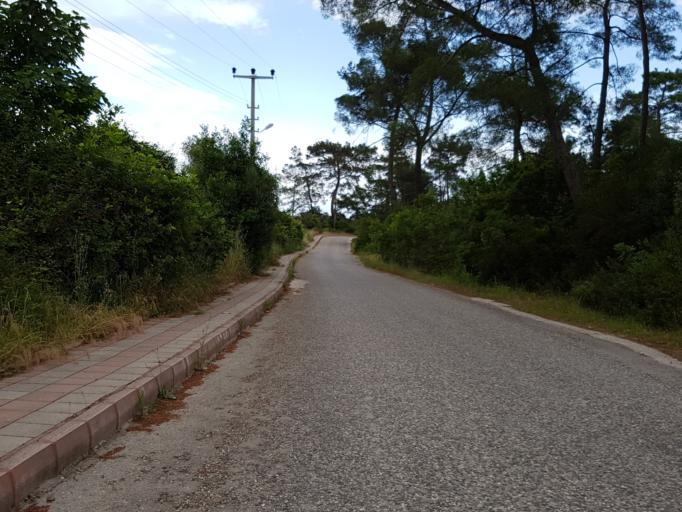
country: TR
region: Antalya
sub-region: Kemer
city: Goeynuek
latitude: 36.6437
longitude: 30.5491
